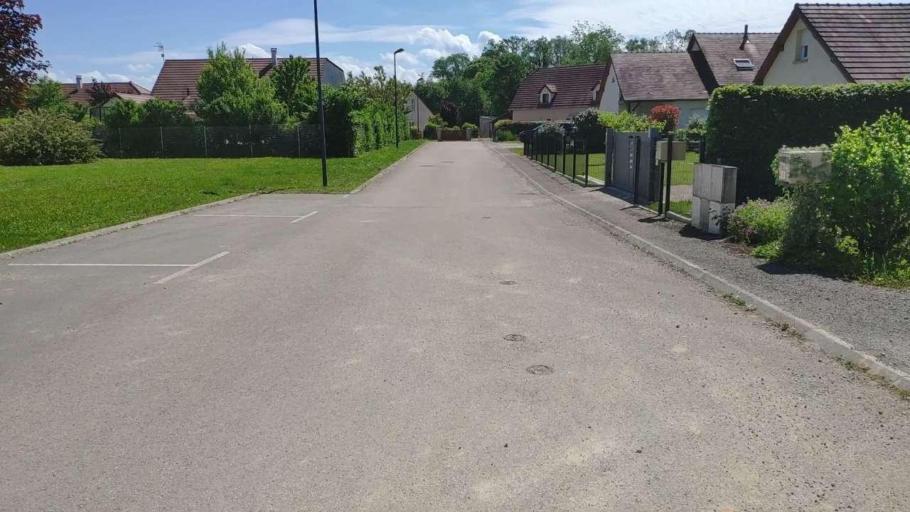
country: FR
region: Franche-Comte
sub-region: Departement du Jura
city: Bletterans
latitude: 46.7333
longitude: 5.4557
